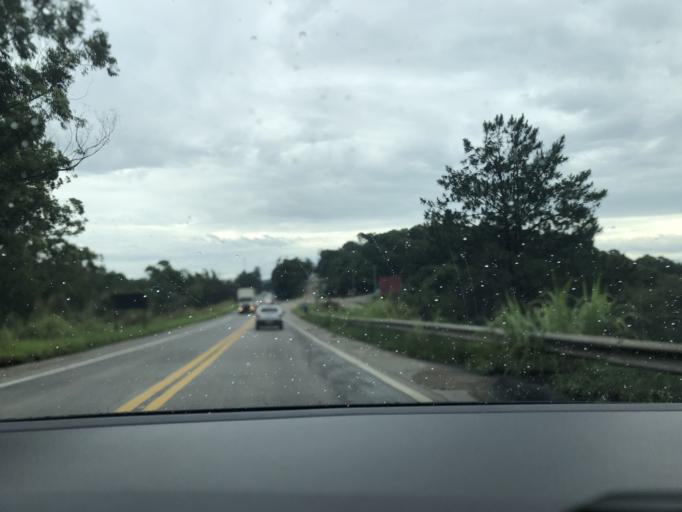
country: BR
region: Sao Paulo
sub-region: Campo Limpo Paulista
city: Campo Limpo Paulista
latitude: -23.1622
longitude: -46.7545
